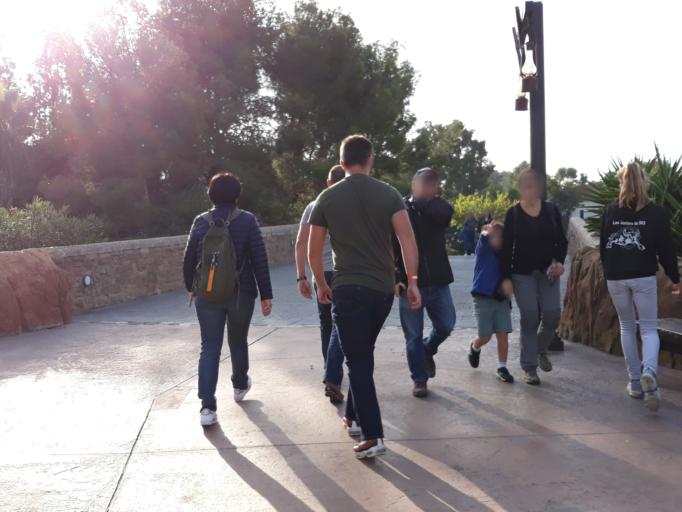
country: ES
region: Catalonia
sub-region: Provincia de Tarragona
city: Salou
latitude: 41.0860
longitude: 1.1567
